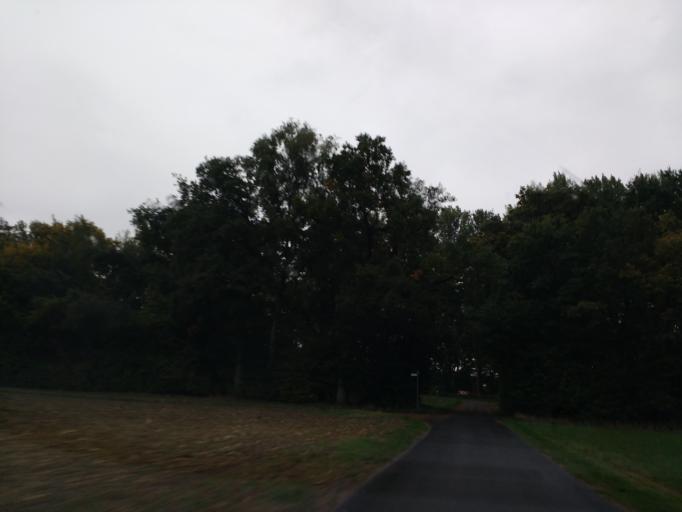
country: DE
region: North Rhine-Westphalia
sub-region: Regierungsbezirk Arnsberg
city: Lippstadt
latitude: 51.7199
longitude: 8.3993
